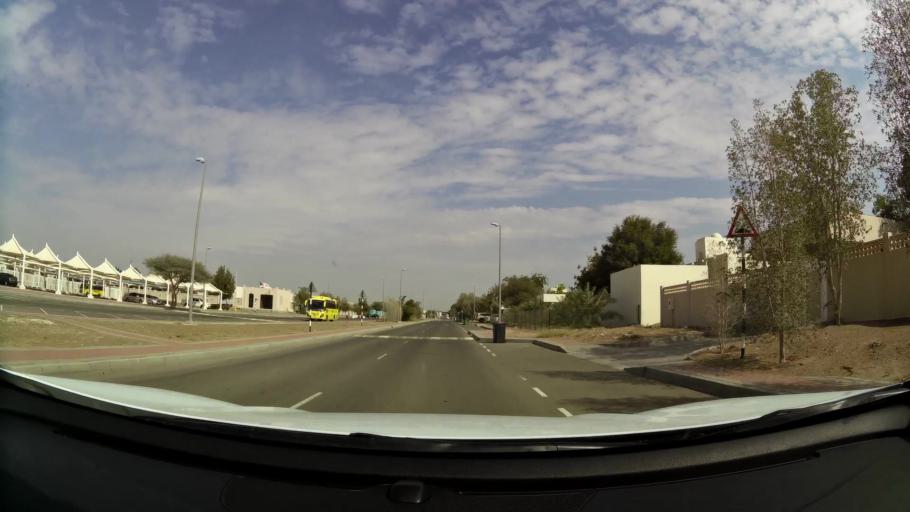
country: AE
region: Abu Dhabi
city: Al Ain
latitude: 24.0985
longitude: 55.9063
